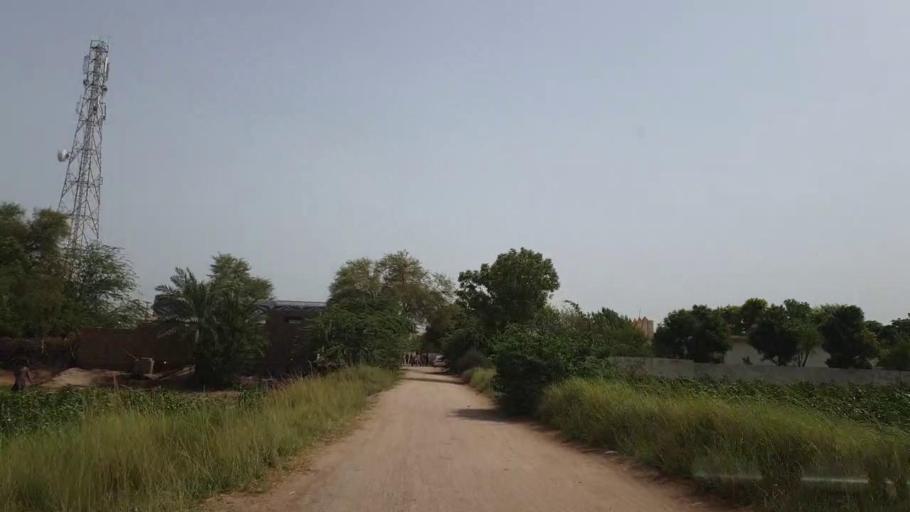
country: PK
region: Sindh
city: Sakrand
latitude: 26.1150
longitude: 68.3977
